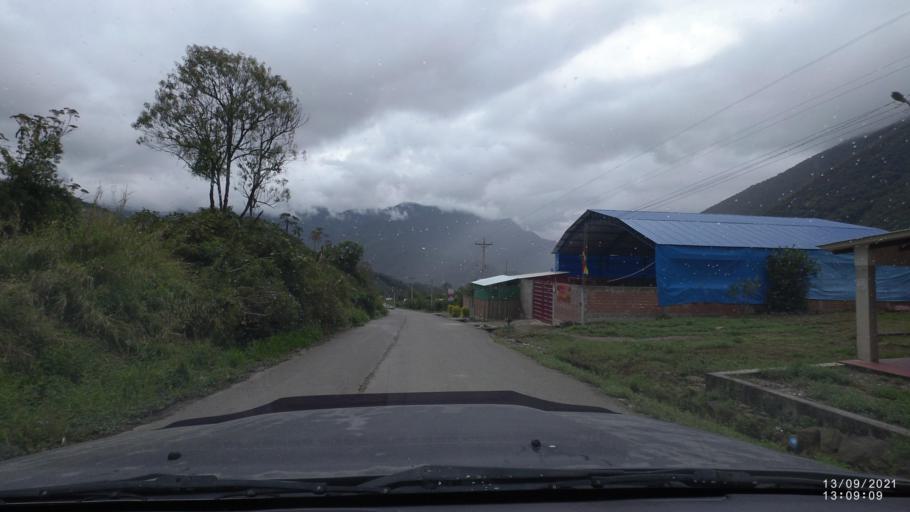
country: BO
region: Cochabamba
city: Colomi
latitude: -17.2125
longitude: -65.8250
